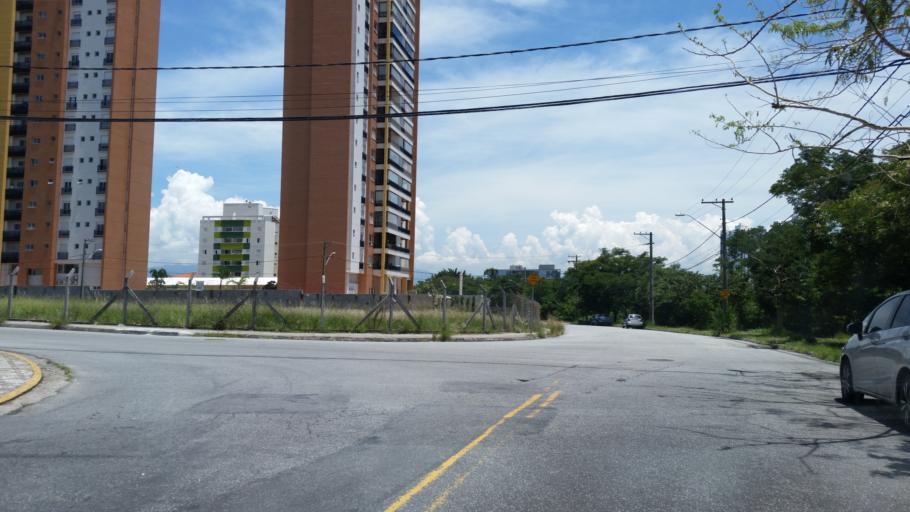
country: BR
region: Sao Paulo
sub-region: Taubate
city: Taubate
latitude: -23.0296
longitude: -45.5771
